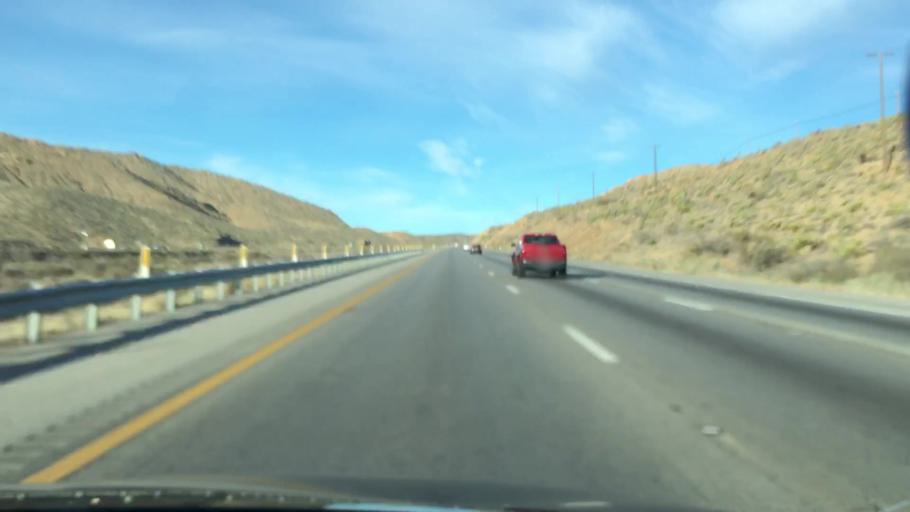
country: US
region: Nevada
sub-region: Clark County
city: Sandy Valley
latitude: 35.4684
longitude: -115.4894
